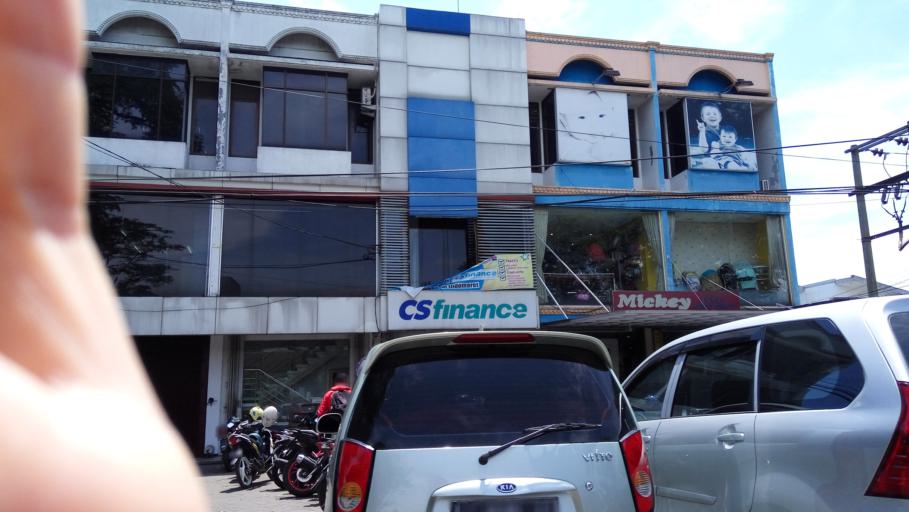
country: ID
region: East Java
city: Malang
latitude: -7.9430
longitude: 112.6415
